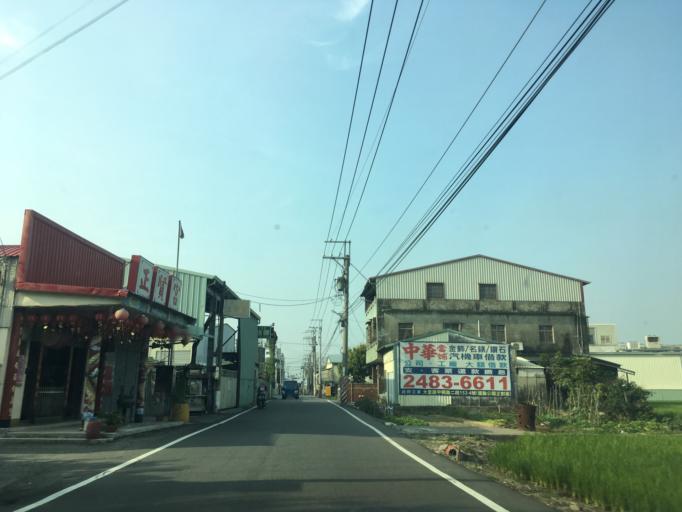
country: TW
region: Taiwan
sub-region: Taichung City
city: Taichung
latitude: 24.0676
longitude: 120.6800
